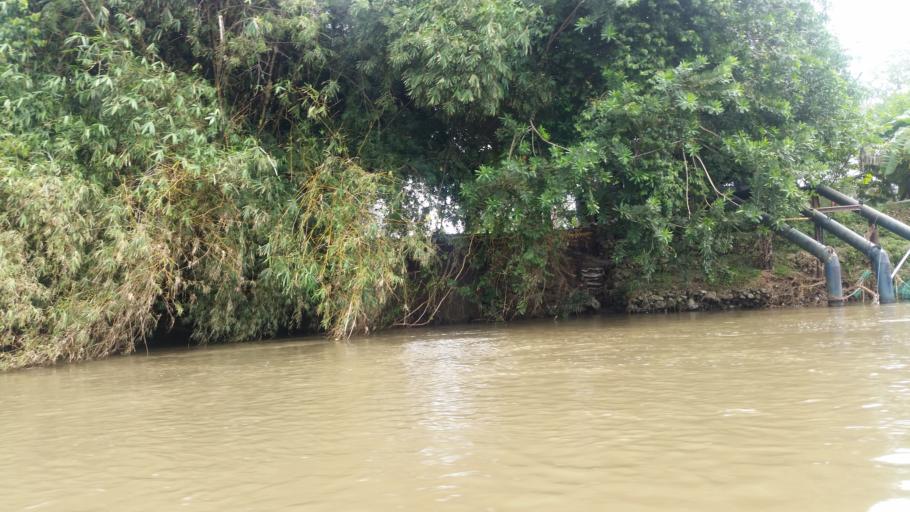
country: CO
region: Magdalena
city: Santa Marta
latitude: 11.2554
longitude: -73.7636
